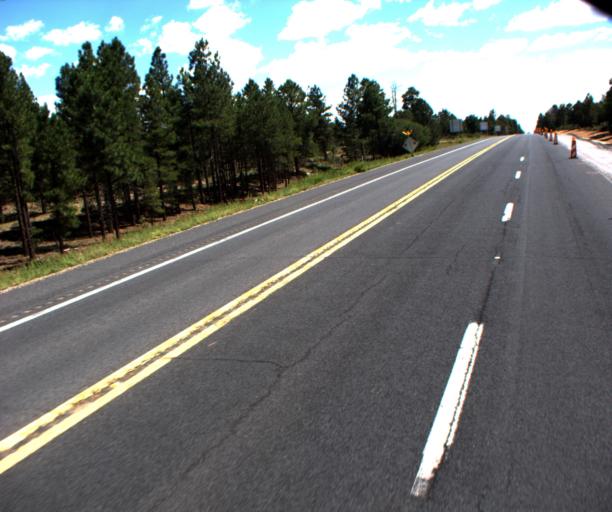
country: US
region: Arizona
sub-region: Coconino County
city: Grand Canyon Village
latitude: 35.9540
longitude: -112.1318
